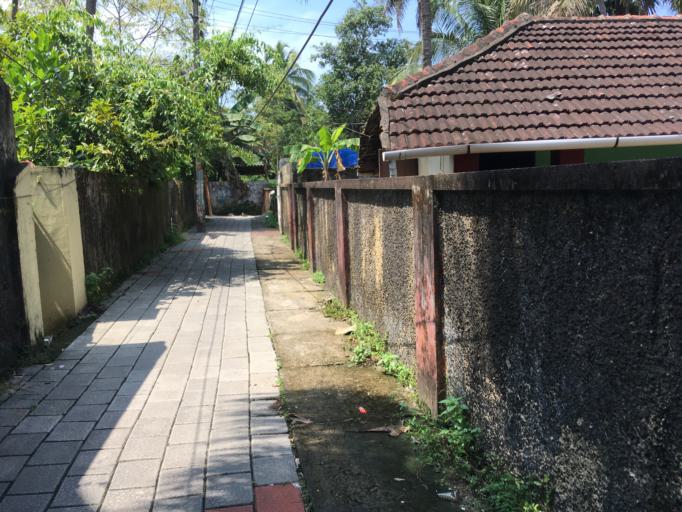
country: IN
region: Kerala
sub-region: Ernakulam
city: Cochin
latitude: 9.9583
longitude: 76.2433
